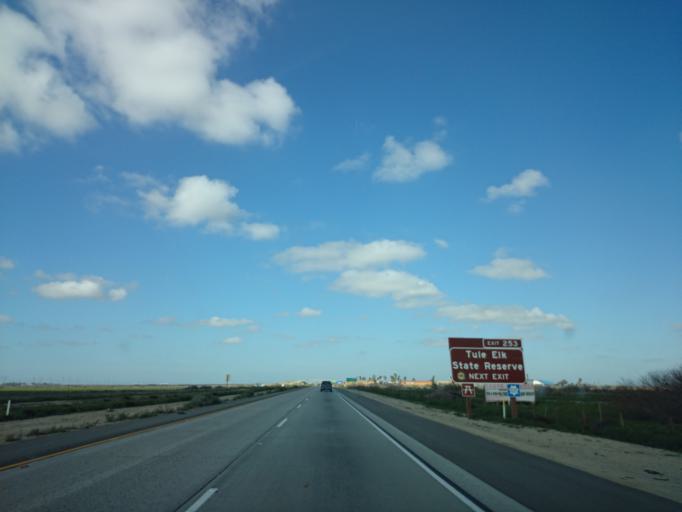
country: US
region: California
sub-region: Kern County
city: Buttonwillow
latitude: 35.3476
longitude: -119.3254
